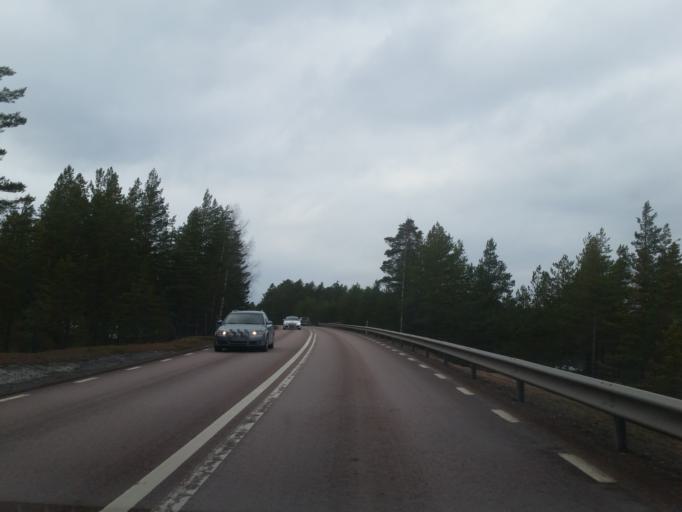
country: SE
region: Dalarna
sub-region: Mora Kommun
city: Mora
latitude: 61.0481
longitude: 14.4883
